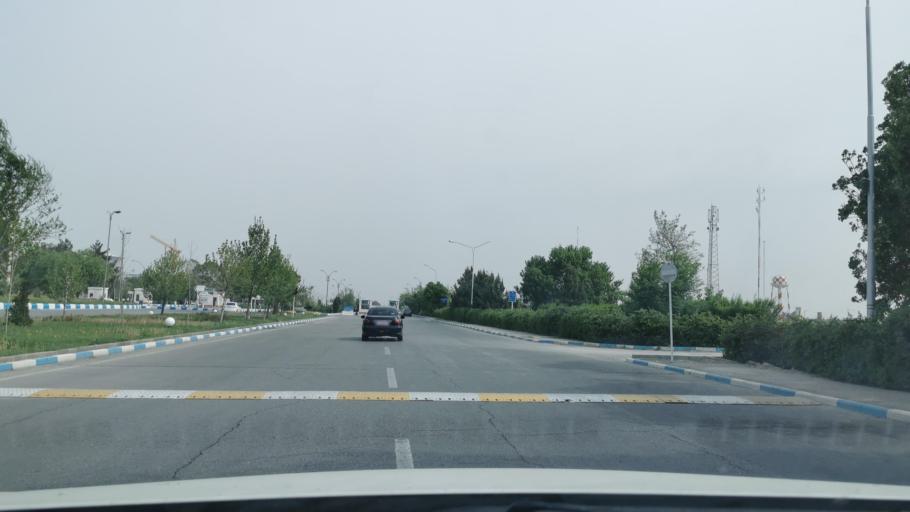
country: IR
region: Razavi Khorasan
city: Mashhad
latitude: 36.2305
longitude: 59.6364
